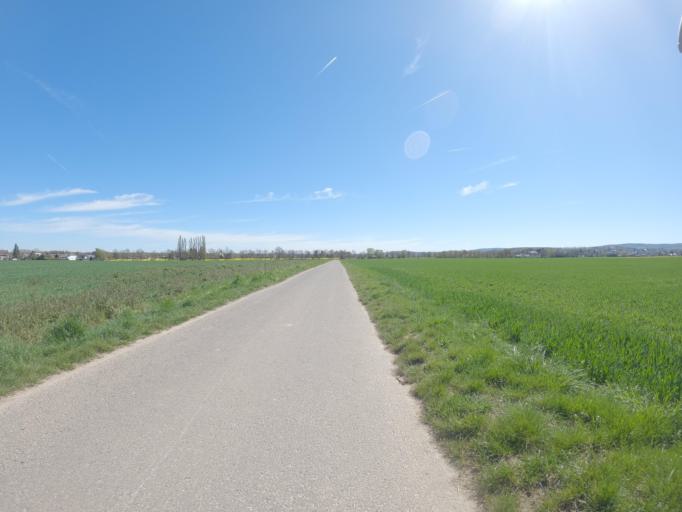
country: DE
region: North Rhine-Westphalia
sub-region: Regierungsbezirk Koln
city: Dueren
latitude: 50.7851
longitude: 6.4576
